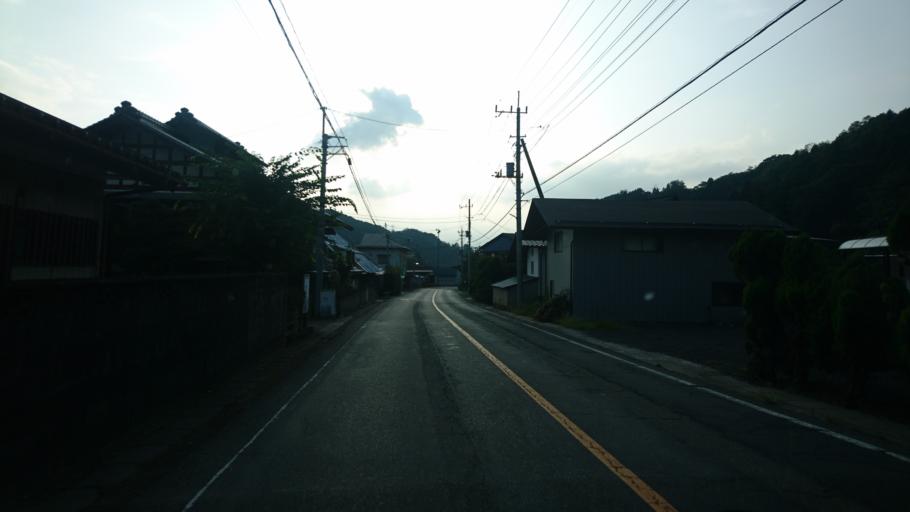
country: JP
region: Gunma
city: Numata
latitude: 36.6561
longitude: 139.1283
